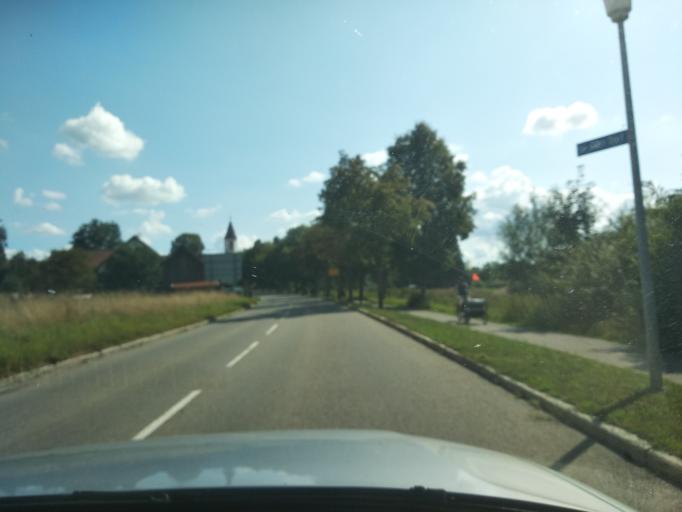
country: DE
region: Baden-Wuerttemberg
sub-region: Tuebingen Region
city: Leutkirch im Allgau
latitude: 47.8608
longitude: 10.0007
